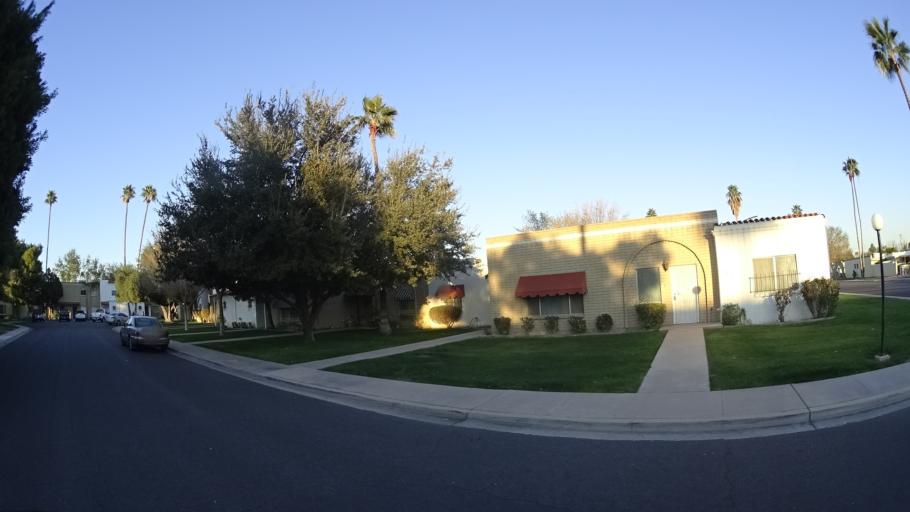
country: US
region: Arizona
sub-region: Maricopa County
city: Mesa
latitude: 33.4262
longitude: -111.8198
